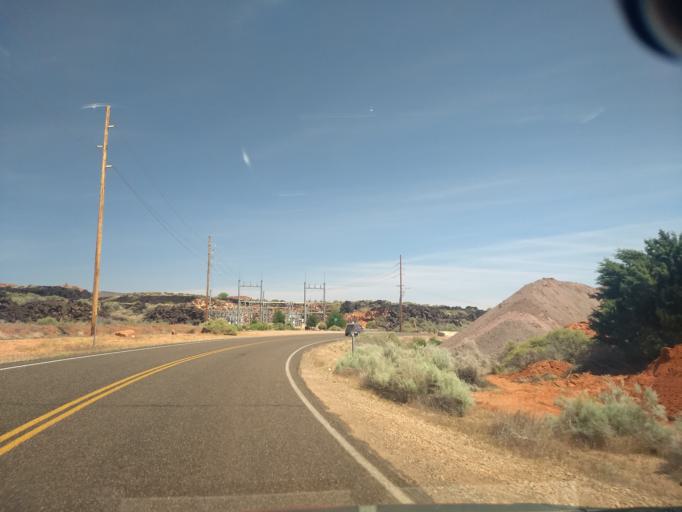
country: US
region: Utah
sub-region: Washington County
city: Santa Clara
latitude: 37.1467
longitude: -113.6551
